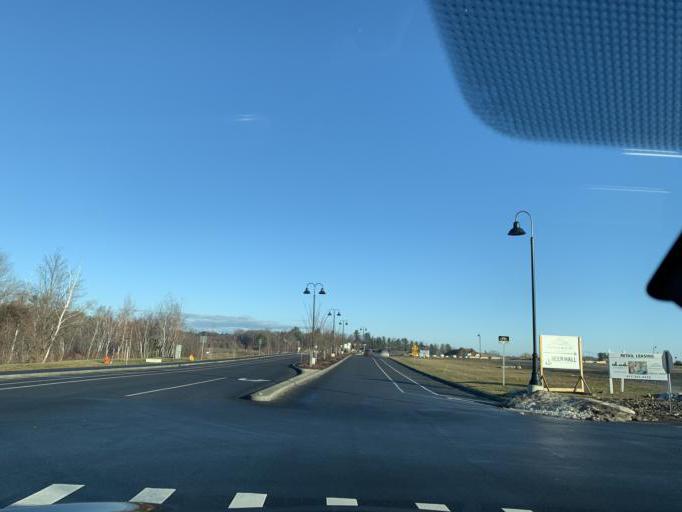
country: US
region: New Hampshire
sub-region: Rockingham County
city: Londonderry
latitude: 42.8708
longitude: -71.3500
